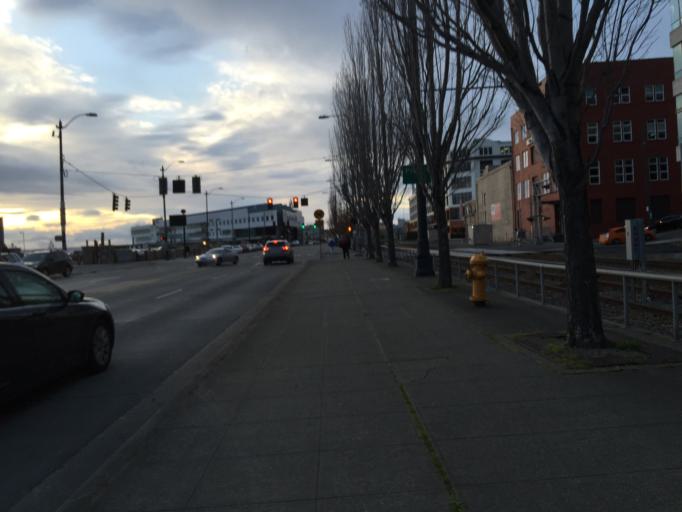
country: US
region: Washington
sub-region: King County
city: Seattle
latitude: 47.6126
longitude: -122.3505
